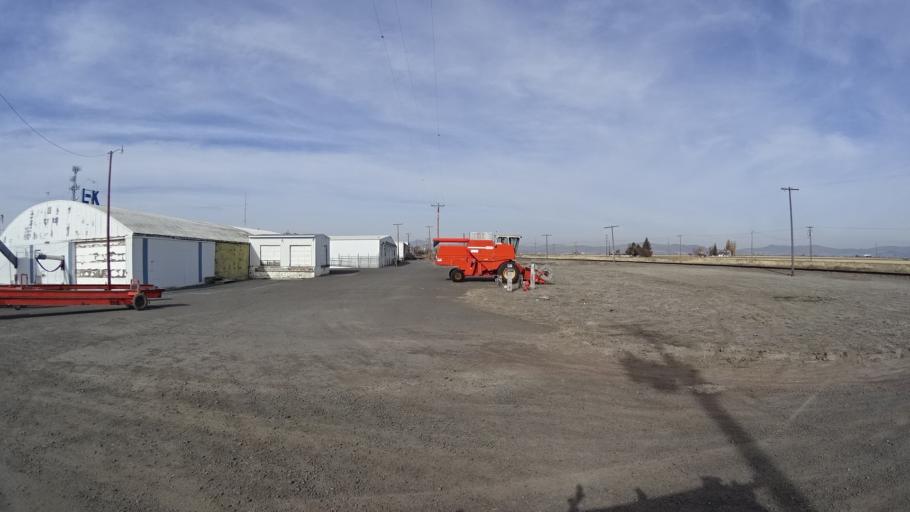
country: US
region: California
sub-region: Siskiyou County
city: Tulelake
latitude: 41.9500
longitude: -121.4671
